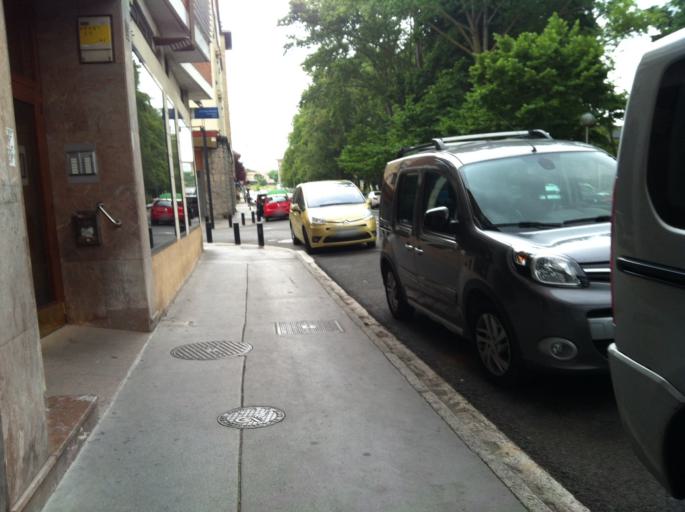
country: ES
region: Basque Country
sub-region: Provincia de Alava
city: Gasteiz / Vitoria
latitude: 42.8374
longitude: -2.6724
